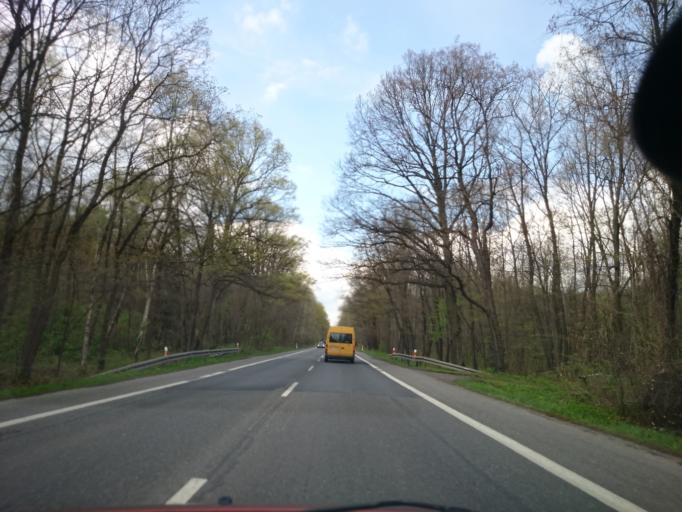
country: PL
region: Opole Voivodeship
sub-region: Powiat opolski
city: Tarnow Opolski
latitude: 50.5920
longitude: 18.0967
